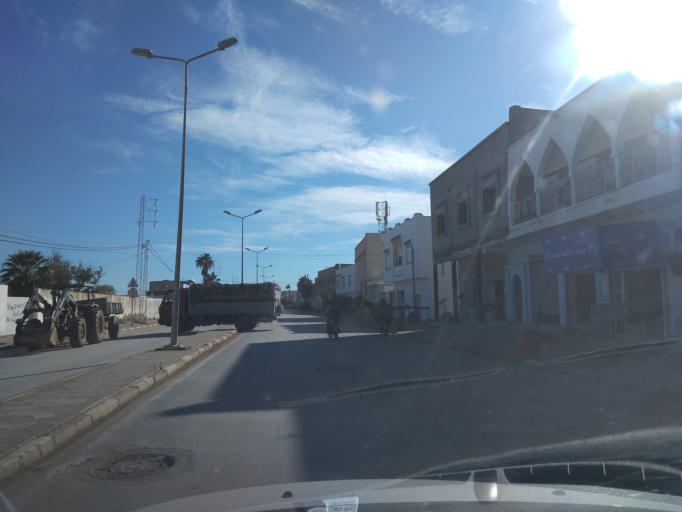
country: TN
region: Ariana
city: Qal'at al Andalus
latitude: 37.0573
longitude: 10.1202
